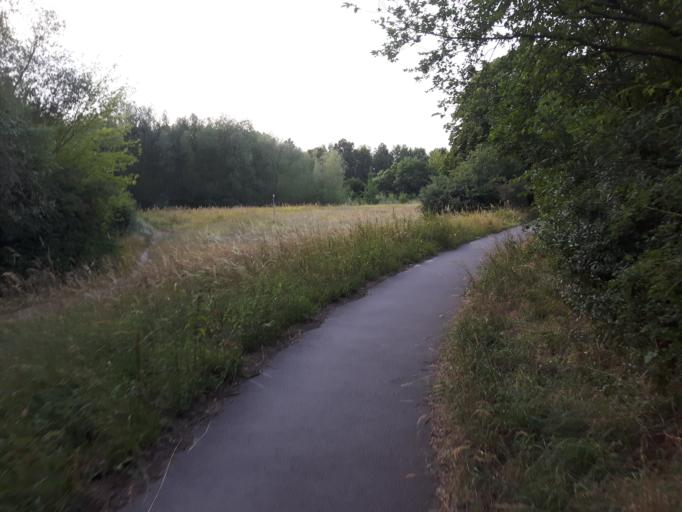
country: DE
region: Berlin
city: Staaken
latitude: 52.5509
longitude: 13.1462
